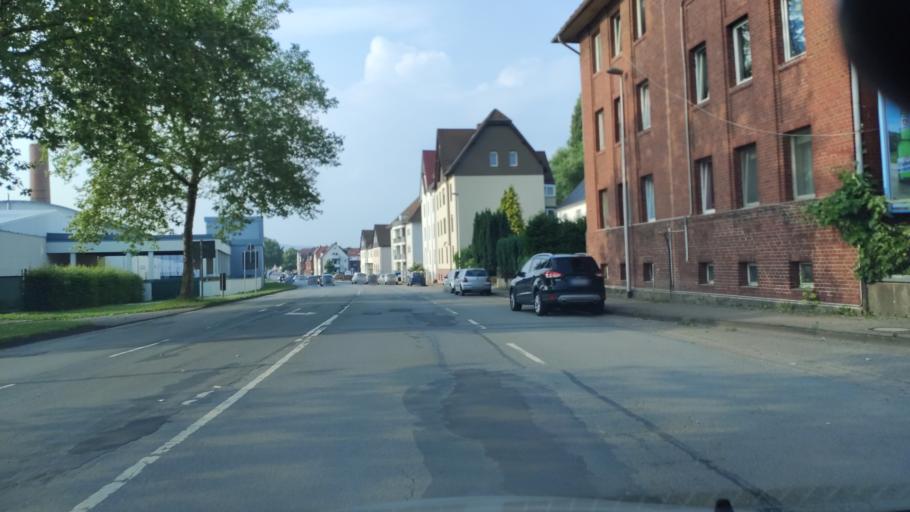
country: DE
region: Lower Saxony
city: Holzminden
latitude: 51.8149
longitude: 9.4488
